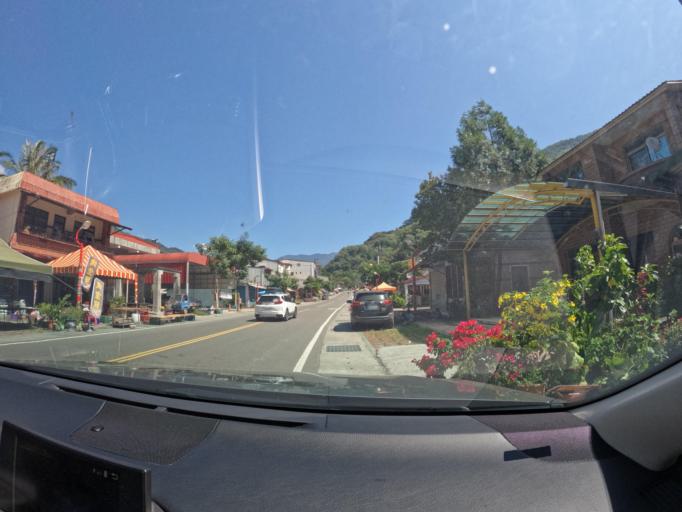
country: TW
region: Taiwan
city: Yujing
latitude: 23.2386
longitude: 120.8117
